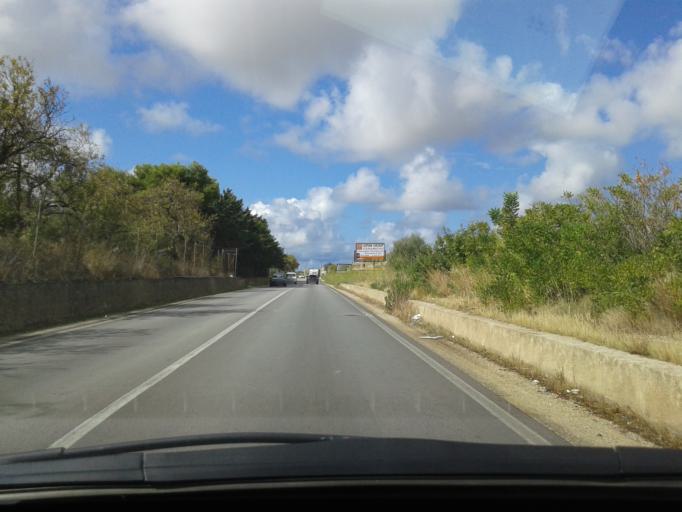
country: IT
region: Sicily
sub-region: Trapani
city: Custonaci
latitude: 38.0801
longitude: 12.7066
